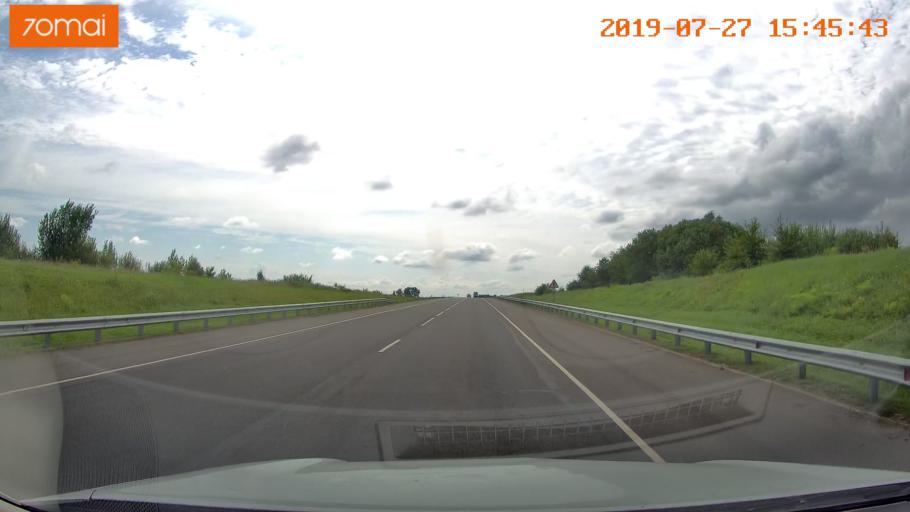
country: RU
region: Kaliningrad
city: Gusev
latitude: 54.6094
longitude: 22.1313
